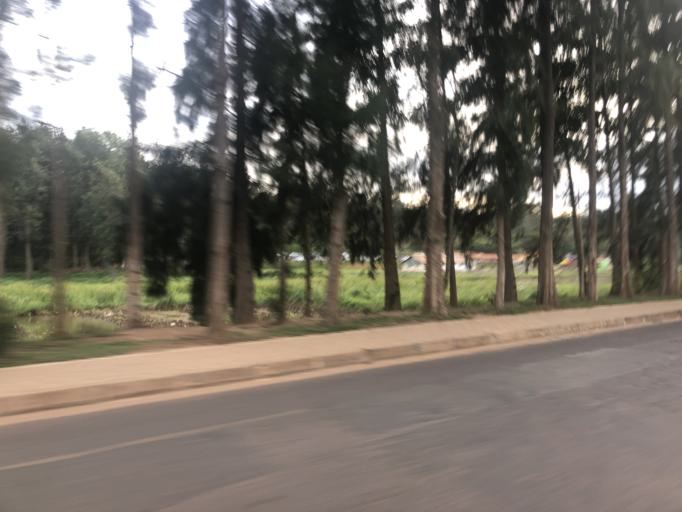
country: RW
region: Kigali
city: Kigali
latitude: -1.9308
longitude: 30.0823
